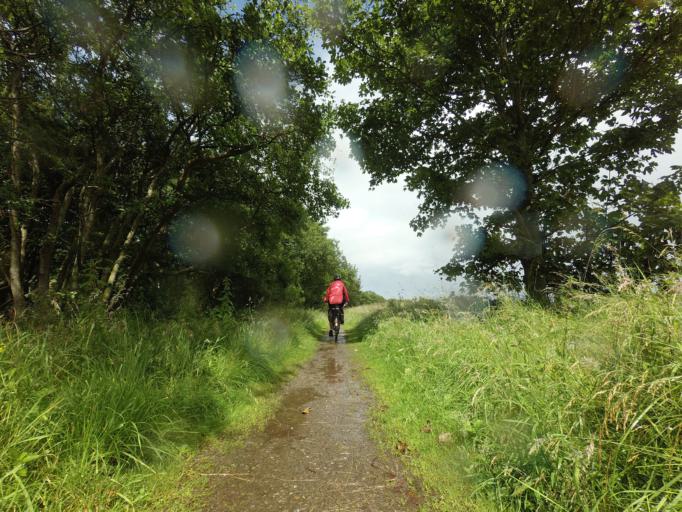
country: GB
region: Scotland
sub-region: Moray
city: Fochabers
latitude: 57.6659
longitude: -3.0912
